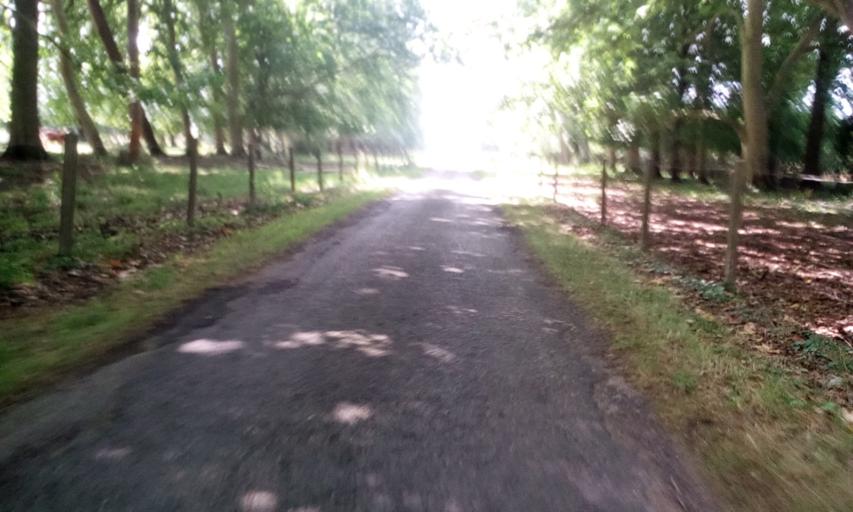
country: FR
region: Lower Normandy
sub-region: Departement du Calvados
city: Bellengreville
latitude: 49.1385
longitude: -0.2218
